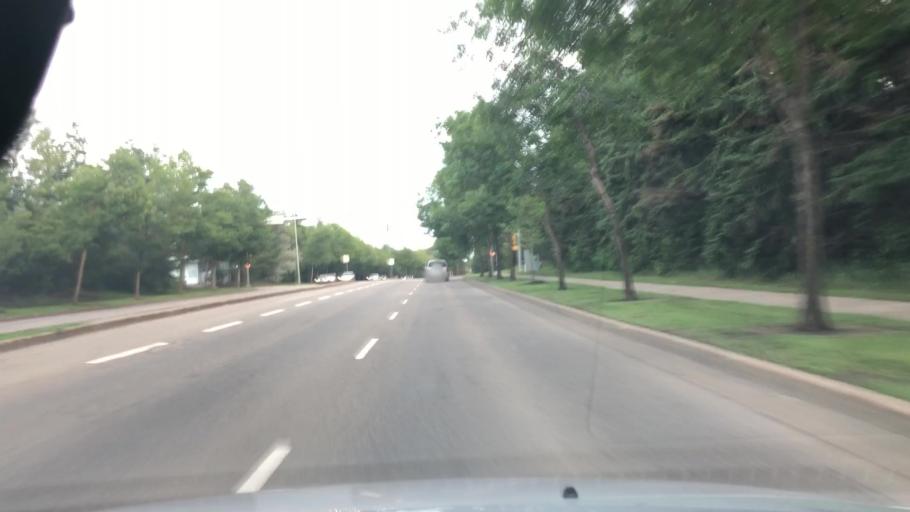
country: CA
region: Alberta
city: St. Albert
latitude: 53.6390
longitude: -113.5953
